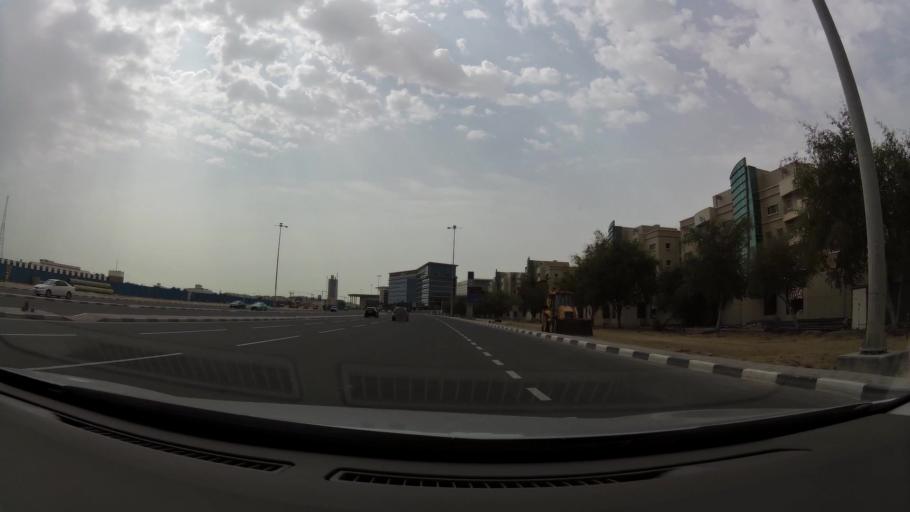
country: QA
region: Baladiyat ad Dawhah
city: Doha
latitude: 25.3007
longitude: 51.5071
